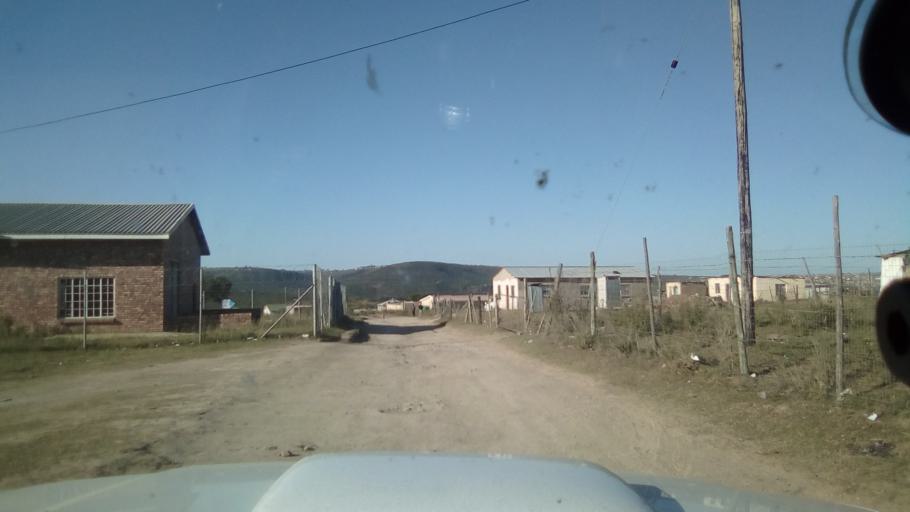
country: ZA
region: Eastern Cape
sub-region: Buffalo City Metropolitan Municipality
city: Bhisho
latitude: -32.8182
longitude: 27.3668
